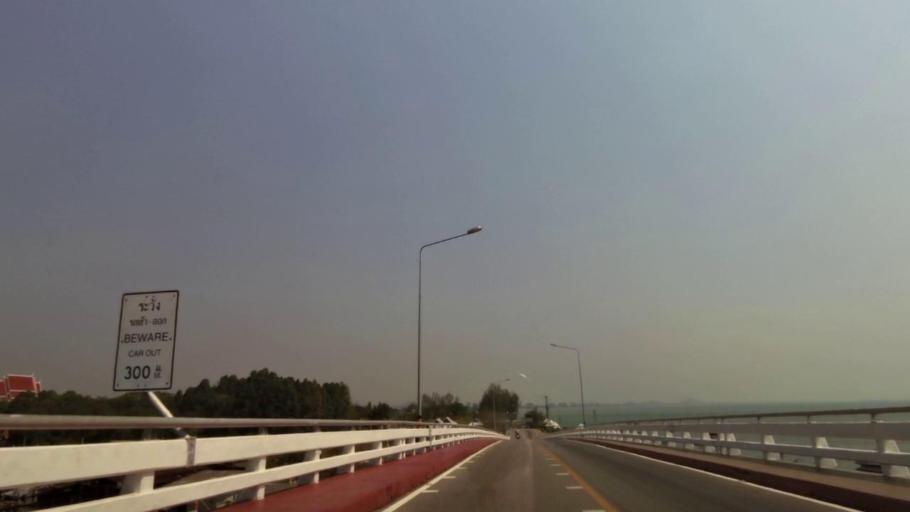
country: TH
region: Chanthaburi
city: Tha Mai
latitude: 12.5391
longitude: 101.9496
